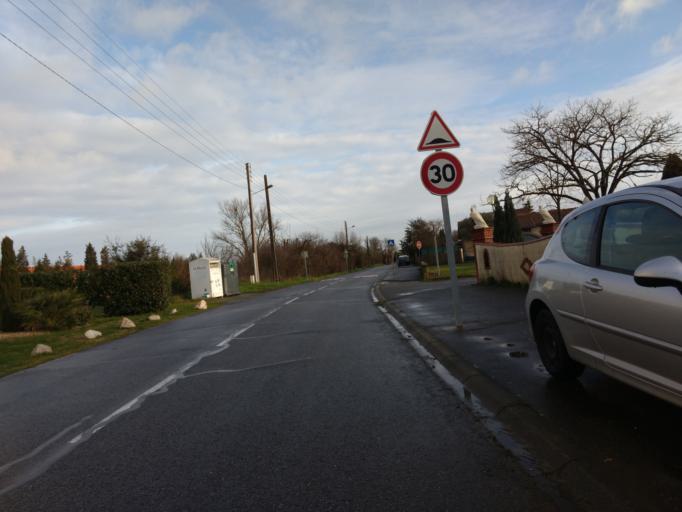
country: FR
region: Midi-Pyrenees
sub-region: Departement de la Haute-Garonne
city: Colomiers
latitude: 43.6095
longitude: 1.3165
